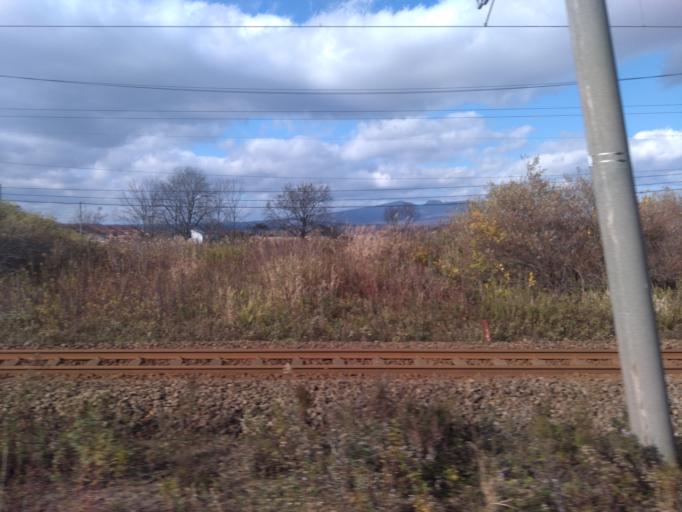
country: JP
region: Hokkaido
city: Shiraoi
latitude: 42.5785
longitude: 141.4164
